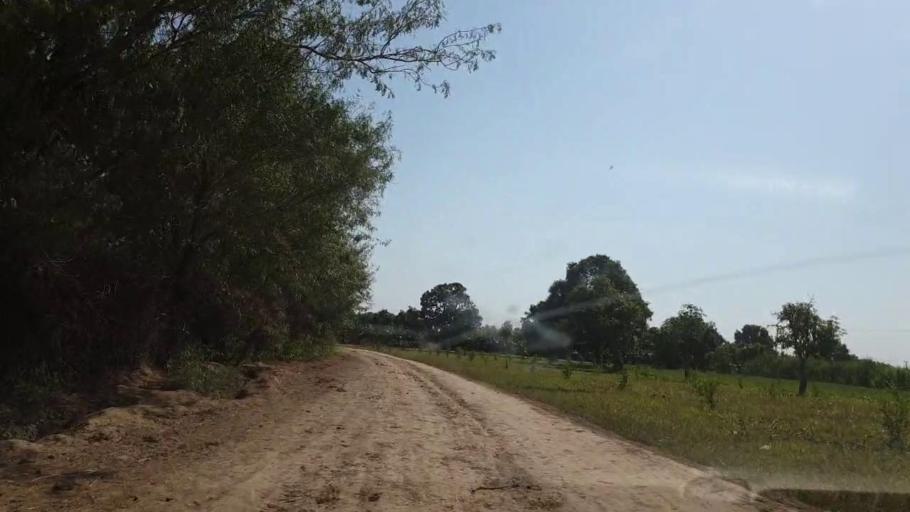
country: PK
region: Sindh
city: Tando Jam
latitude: 25.3784
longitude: 68.5796
